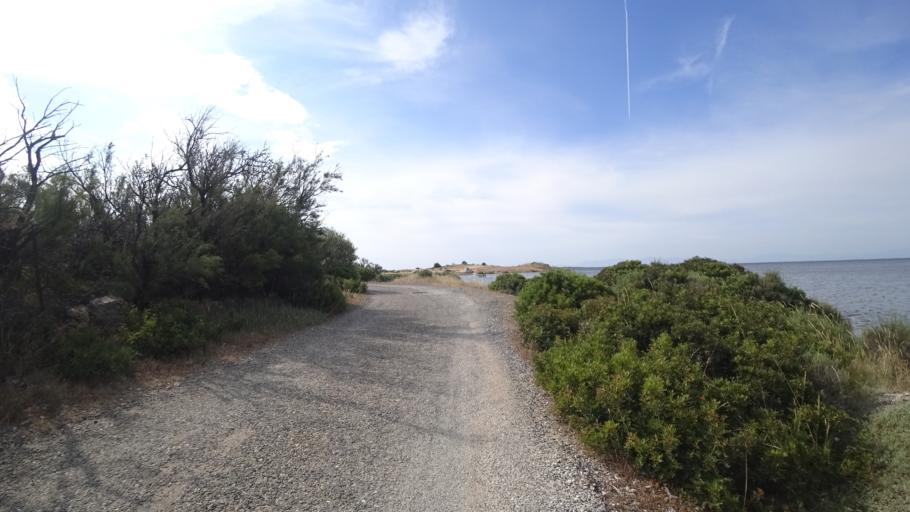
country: FR
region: Languedoc-Roussillon
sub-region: Departement de l'Aude
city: Leucate
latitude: 42.8972
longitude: 3.0285
